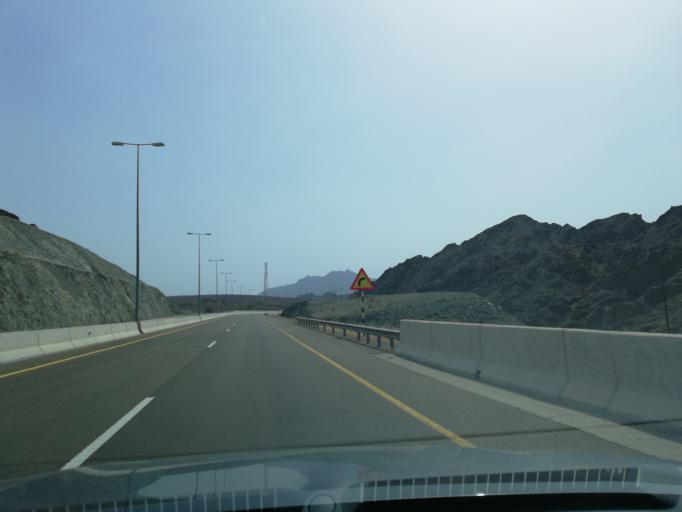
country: OM
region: Al Batinah
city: Al Liwa'
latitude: 24.2634
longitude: 56.3809
